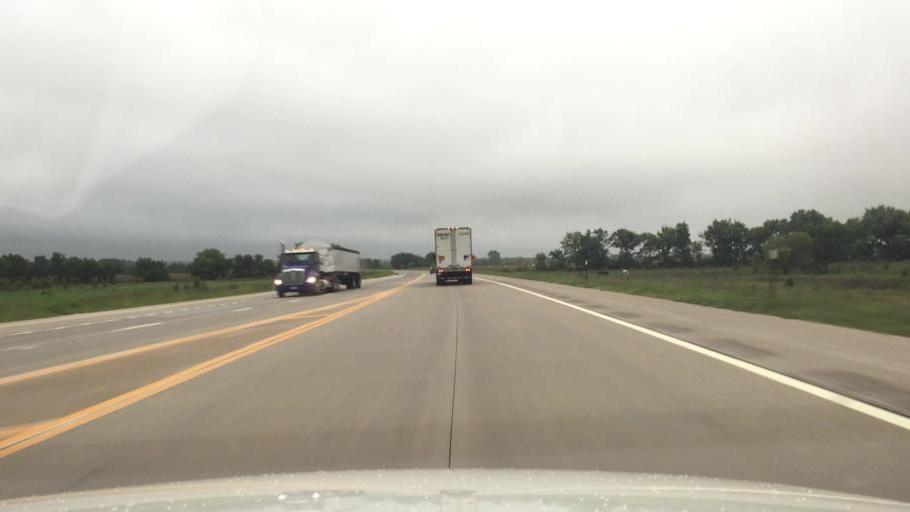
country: US
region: Kansas
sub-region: Montgomery County
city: Cherryvale
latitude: 37.2079
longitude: -95.5849
